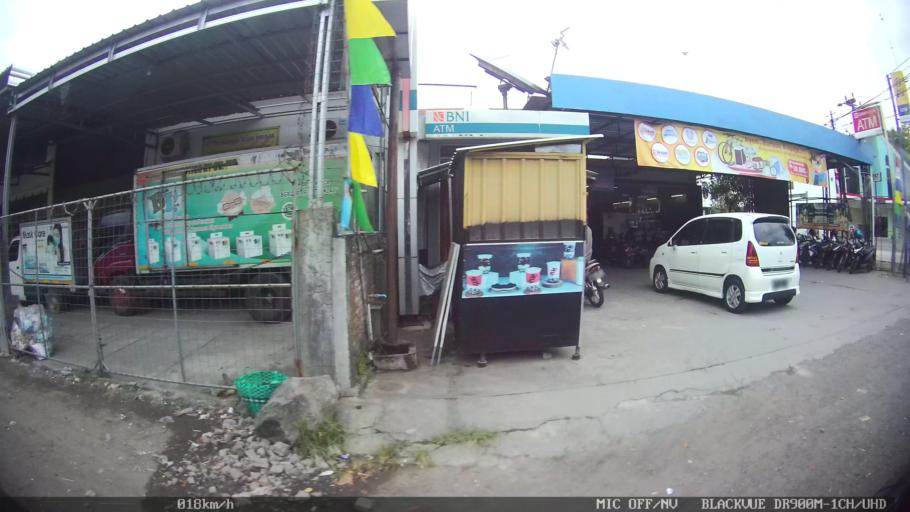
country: ID
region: Daerah Istimewa Yogyakarta
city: Sewon
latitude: -7.8484
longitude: 110.3908
